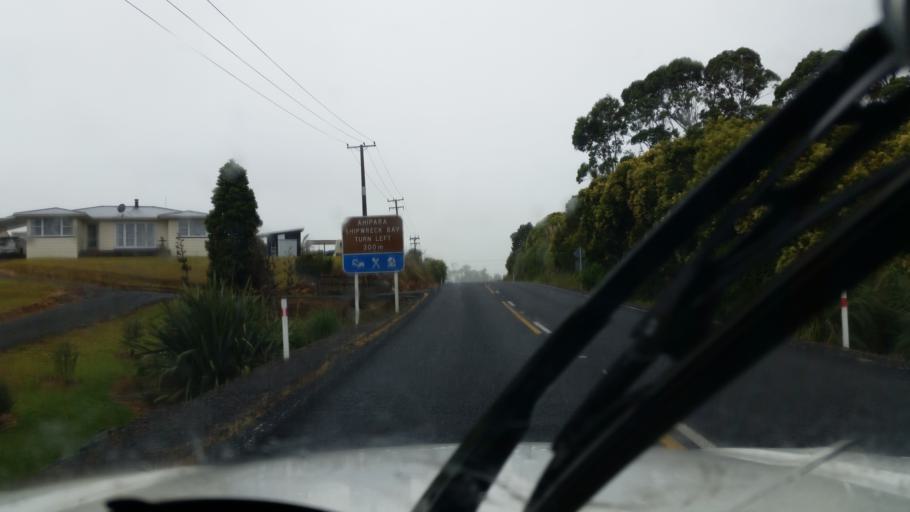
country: NZ
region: Northland
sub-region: Far North District
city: Ahipara
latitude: -35.1737
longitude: 173.1789
